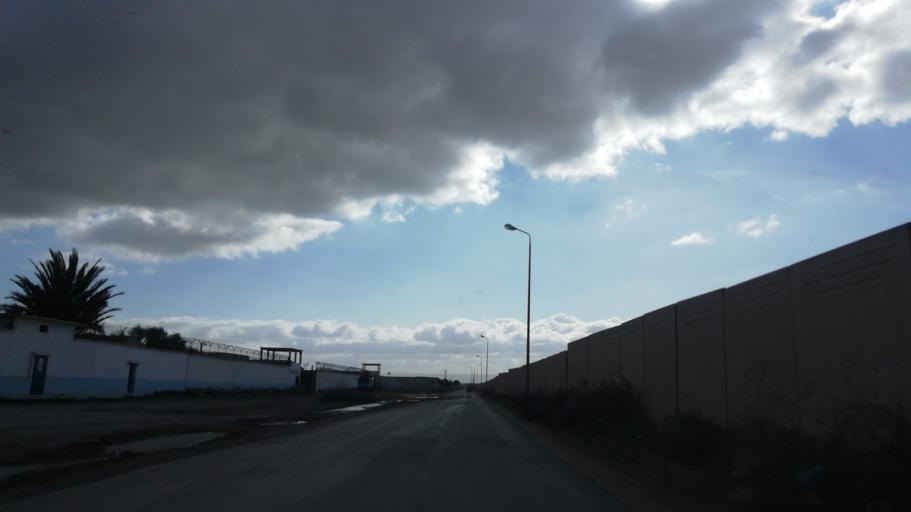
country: DZ
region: Oran
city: Es Senia
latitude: 35.6351
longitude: -0.5968
